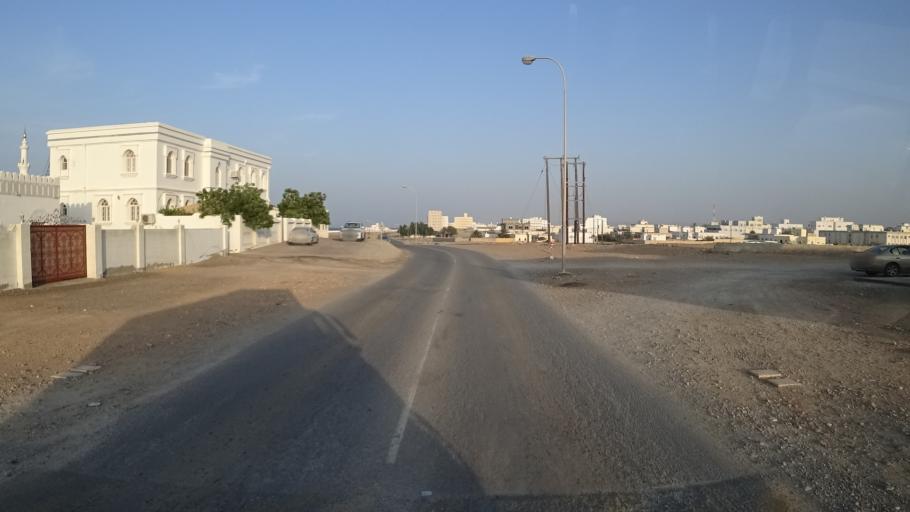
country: OM
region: Ash Sharqiyah
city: Sur
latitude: 22.6110
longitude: 59.4666
